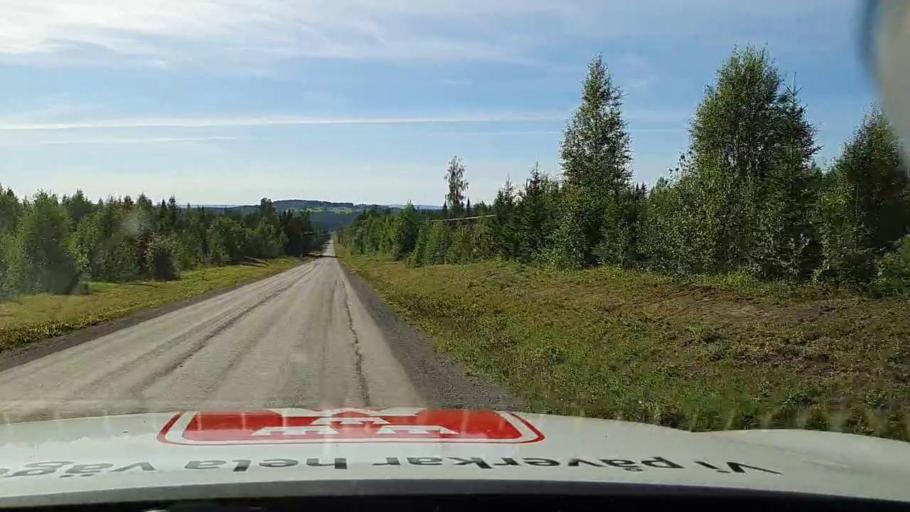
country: SE
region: Jaemtland
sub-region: OEstersunds Kommun
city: Lit
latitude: 63.6789
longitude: 14.7957
